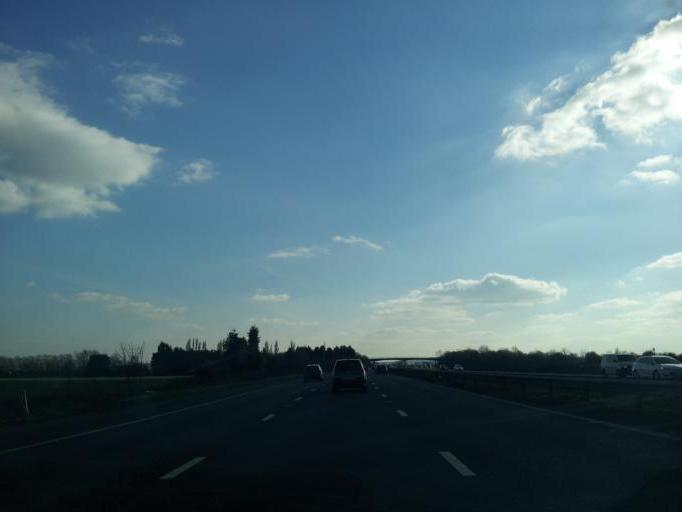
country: GB
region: England
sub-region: North Somerset
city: Kingston Seymour
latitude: 51.4017
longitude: -2.8537
